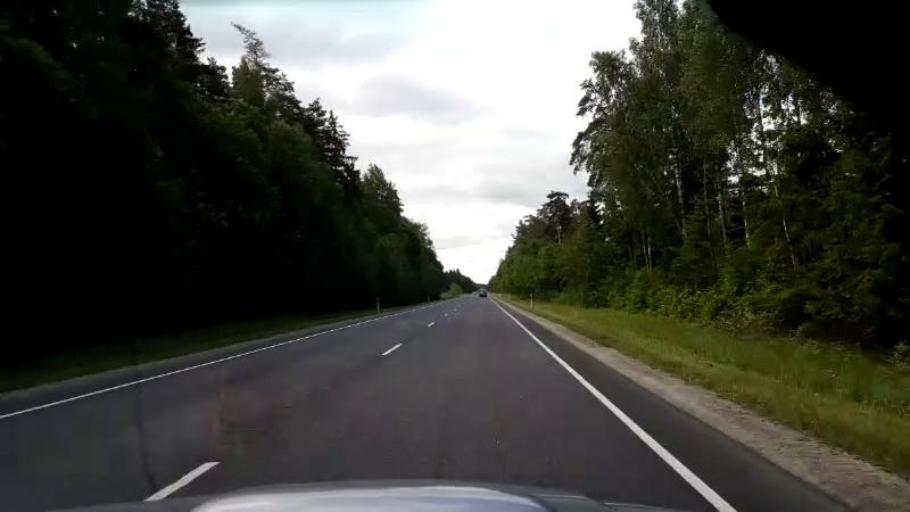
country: EE
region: Raplamaa
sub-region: Maerjamaa vald
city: Marjamaa
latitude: 58.9107
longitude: 24.4563
